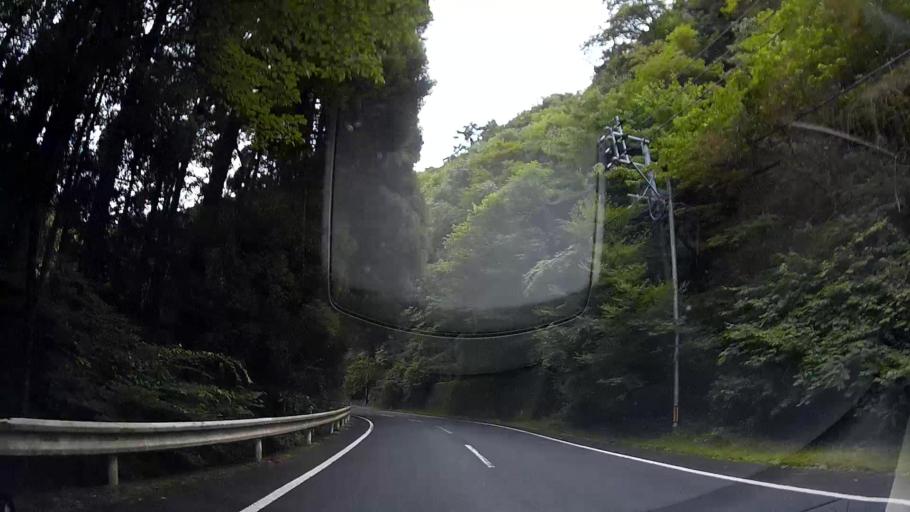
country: JP
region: Kumamoto
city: Kikuchi
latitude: 33.0720
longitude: 130.9214
